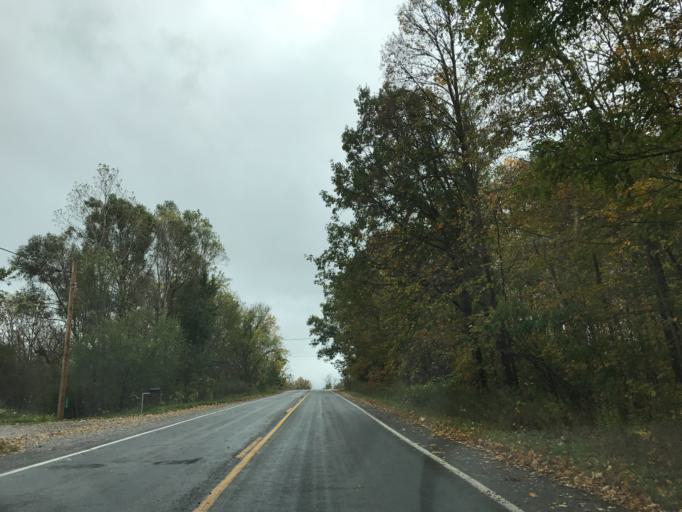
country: US
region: Michigan
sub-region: Washtenaw County
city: Ann Arbor
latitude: 42.3300
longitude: -83.6618
